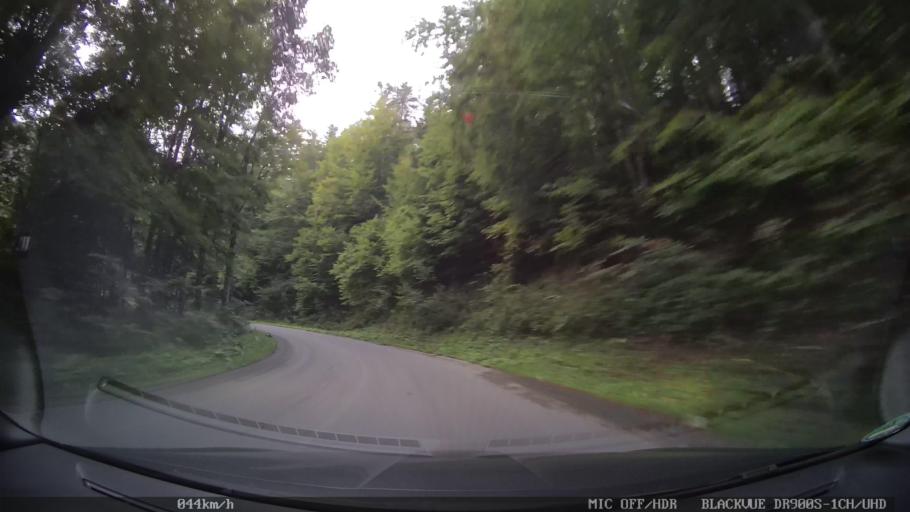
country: HR
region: Primorsko-Goranska
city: Vrbovsko
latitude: 45.2014
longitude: 15.0158
